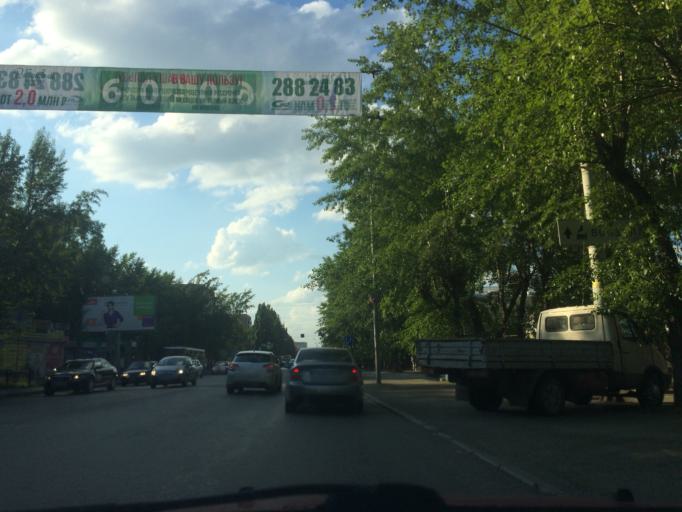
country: RU
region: Sverdlovsk
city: Yekaterinburg
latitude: 56.8294
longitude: 60.6367
